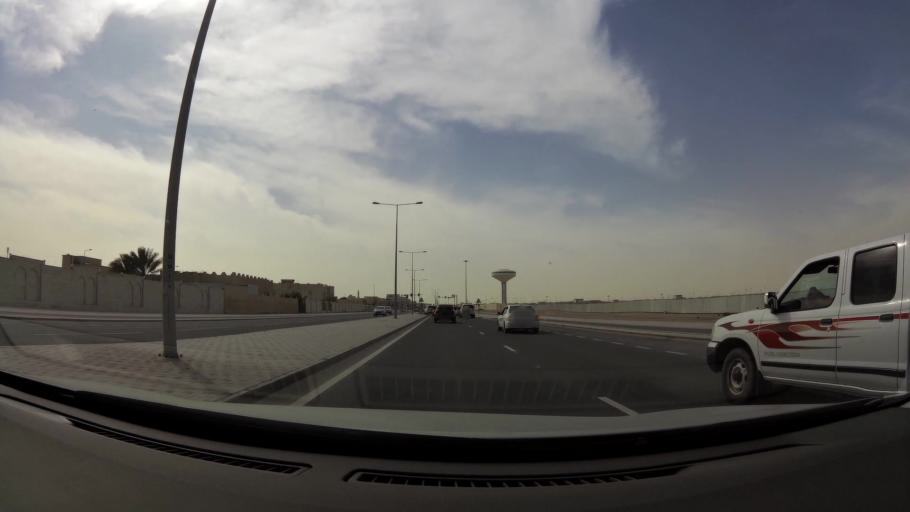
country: QA
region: Baladiyat ar Rayyan
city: Ar Rayyan
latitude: 25.3189
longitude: 51.4077
